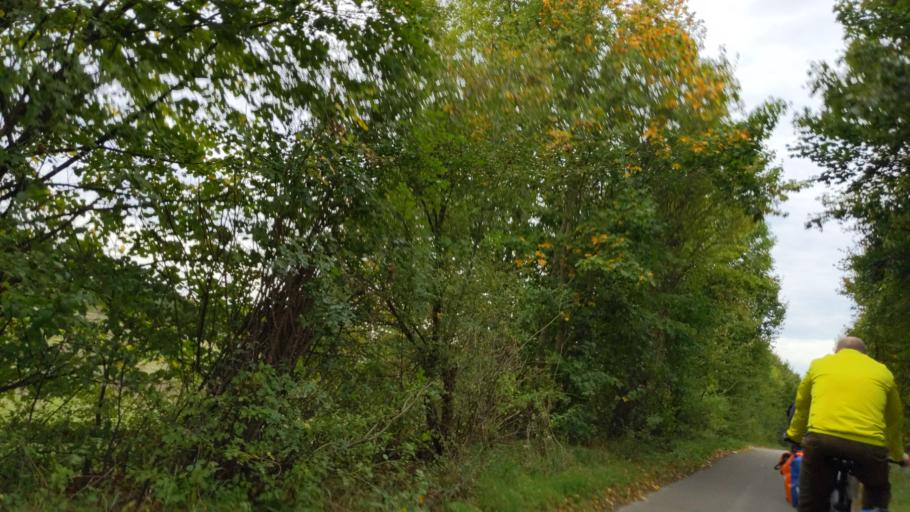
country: DE
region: Schleswig-Holstein
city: Gross Gronau
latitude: 53.8037
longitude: 10.7591
